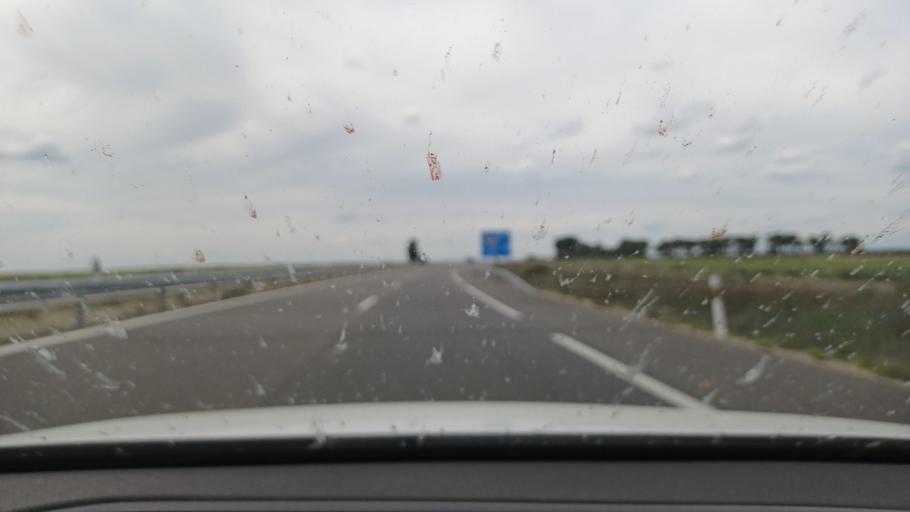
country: ES
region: Castille and Leon
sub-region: Provincia de Valladolid
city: San Miguel del Arroyo
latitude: 41.4306
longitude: -4.4612
